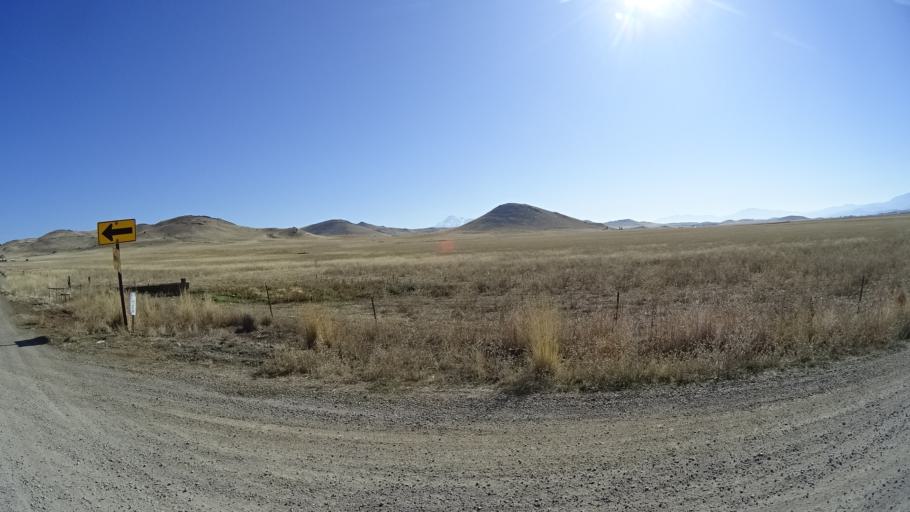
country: US
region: California
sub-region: Siskiyou County
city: Montague
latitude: 41.7865
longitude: -122.4344
